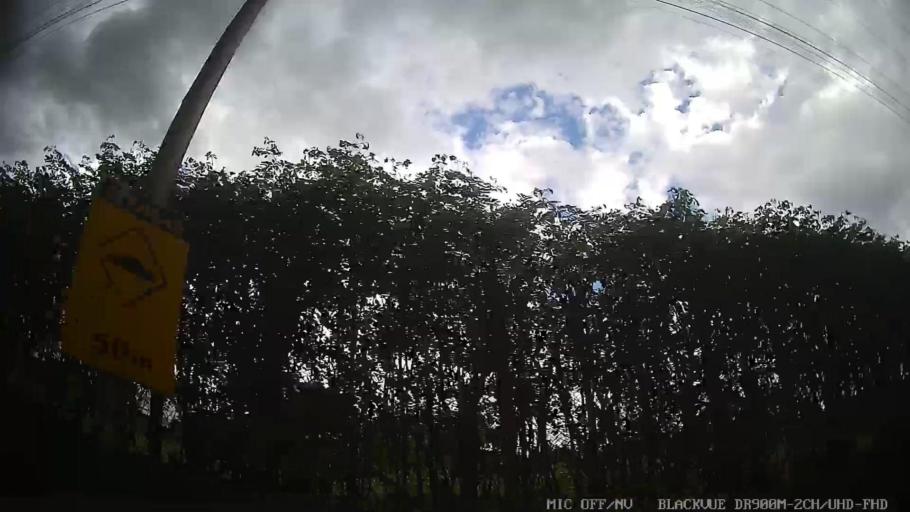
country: BR
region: Sao Paulo
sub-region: Jaguariuna
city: Jaguariuna
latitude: -22.6476
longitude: -47.0628
